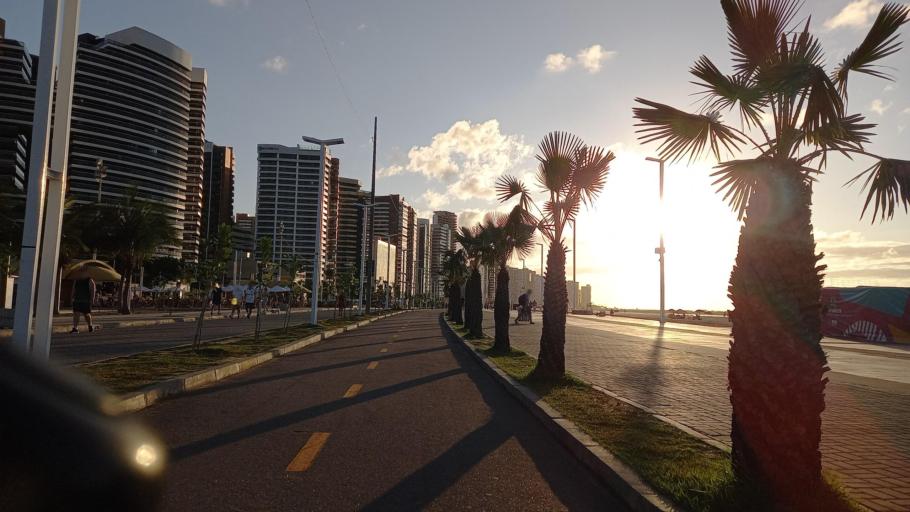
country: BR
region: Ceara
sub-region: Fortaleza
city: Fortaleza
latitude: -3.7249
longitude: -38.4969
